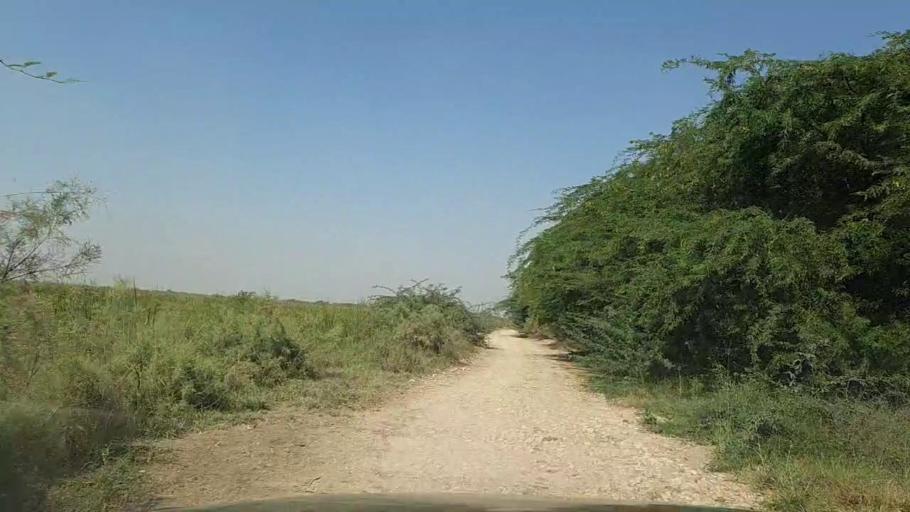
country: PK
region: Sindh
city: Daro Mehar
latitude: 24.8202
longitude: 68.1504
